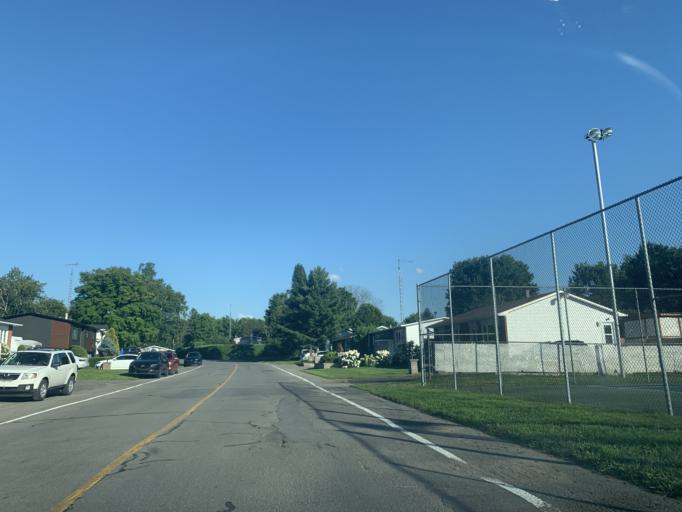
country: CA
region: Ontario
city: Hawkesbury
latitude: 45.6290
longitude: -74.6000
